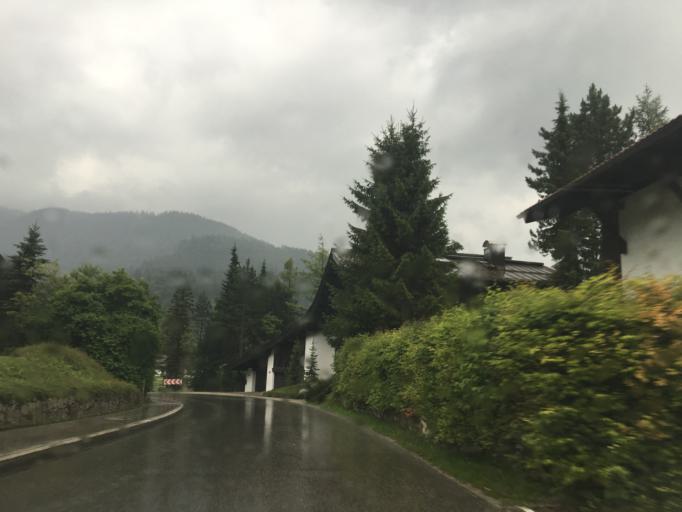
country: DE
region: Bavaria
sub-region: Upper Bavaria
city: Reit im Winkl
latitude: 47.6745
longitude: 12.4882
